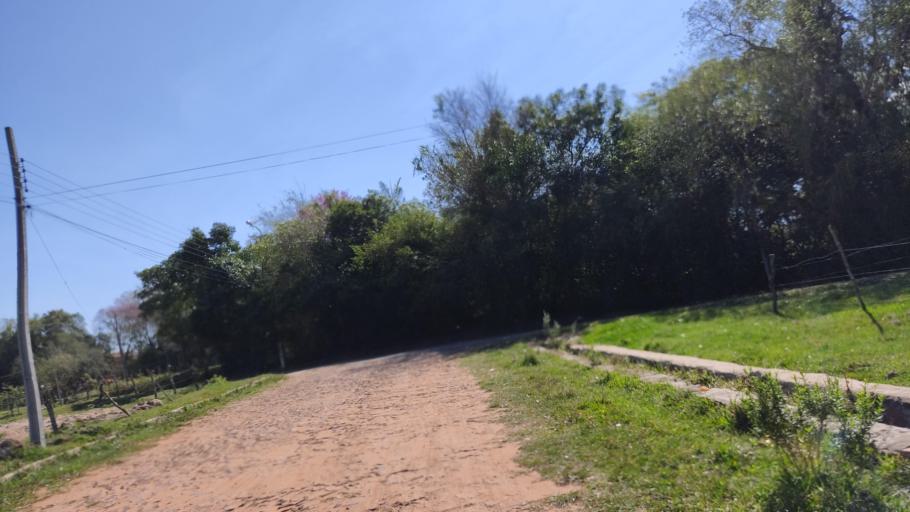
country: PY
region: Misiones
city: San Juan Bautista
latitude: -26.6605
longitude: -57.1397
